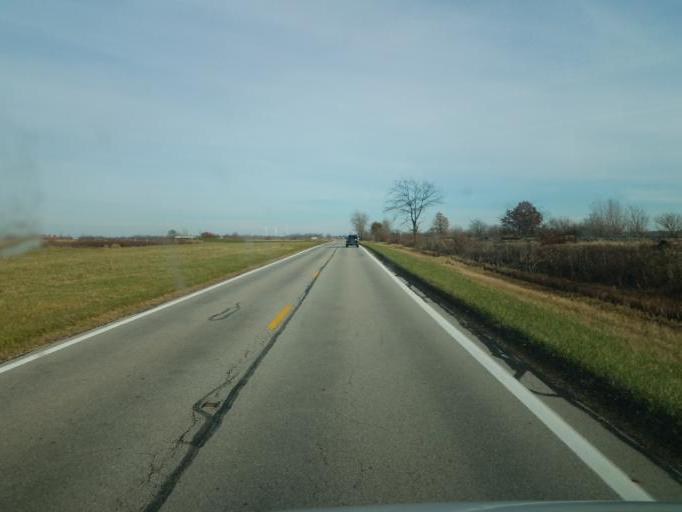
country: US
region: Ohio
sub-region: Marion County
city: Marion
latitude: 40.5862
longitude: -83.2287
